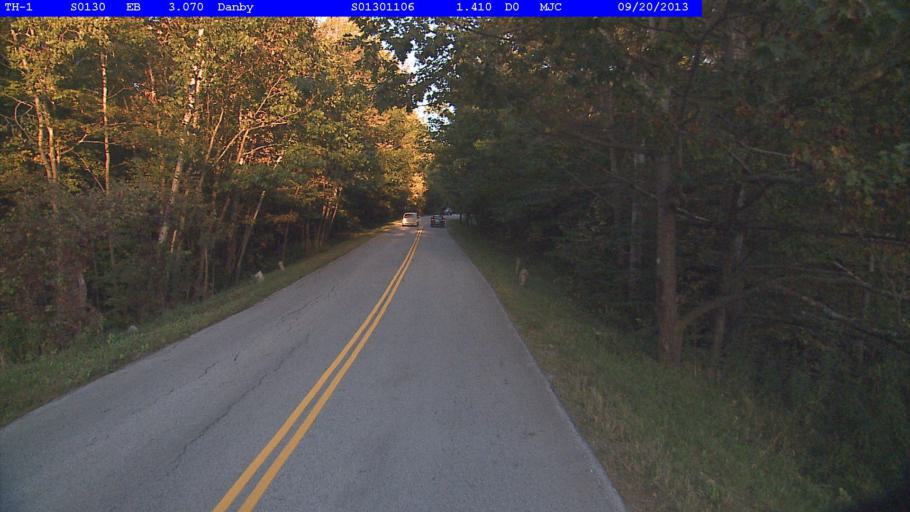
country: US
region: New York
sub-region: Washington County
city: Granville
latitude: 43.3667
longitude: -73.0978
